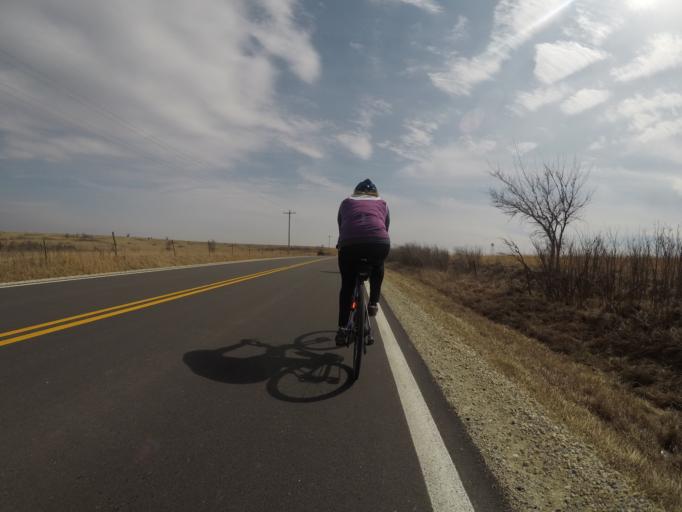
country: US
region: Kansas
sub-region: Geary County
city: Grandview Plaza
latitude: 39.0249
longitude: -96.7662
